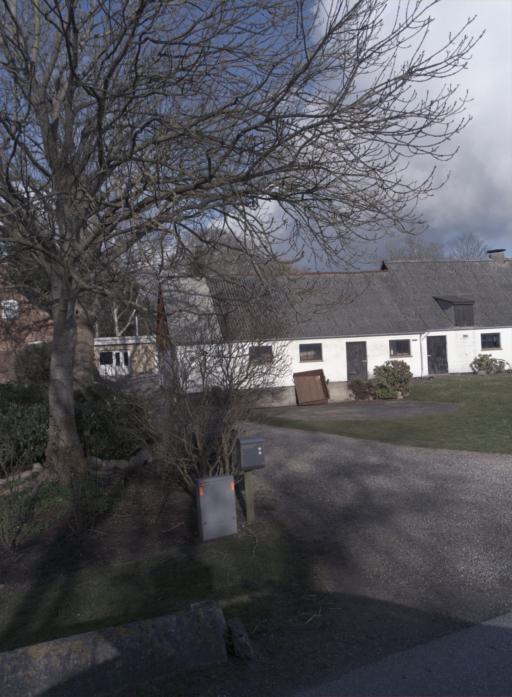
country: DK
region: Zealand
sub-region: Kalundborg Kommune
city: Kalundborg
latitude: 55.6906
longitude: 11.1587
